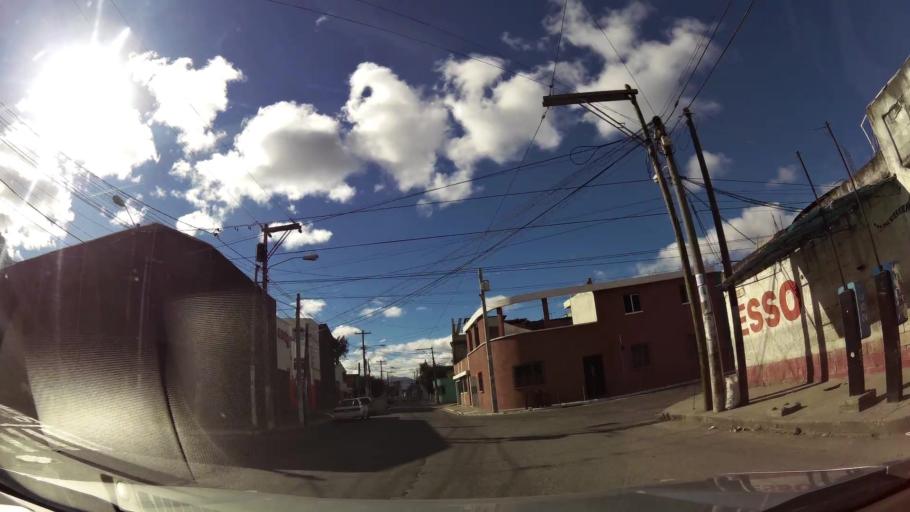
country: GT
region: Guatemala
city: Guatemala City
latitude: 14.6183
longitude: -90.5037
